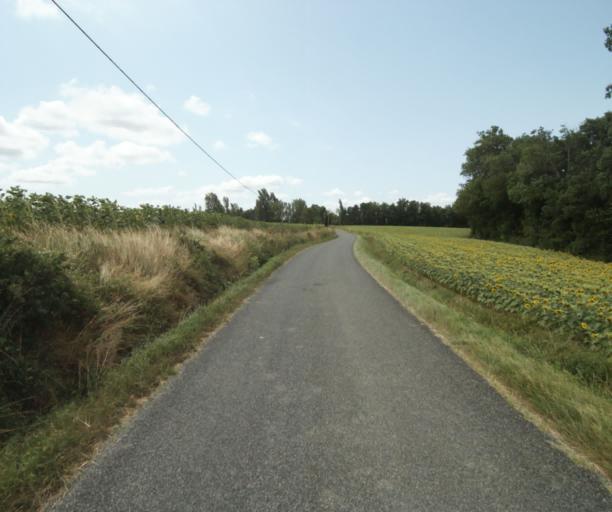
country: FR
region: Midi-Pyrenees
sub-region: Departement de la Haute-Garonne
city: Saint-Felix-Lauragais
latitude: 43.4294
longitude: 1.8987
